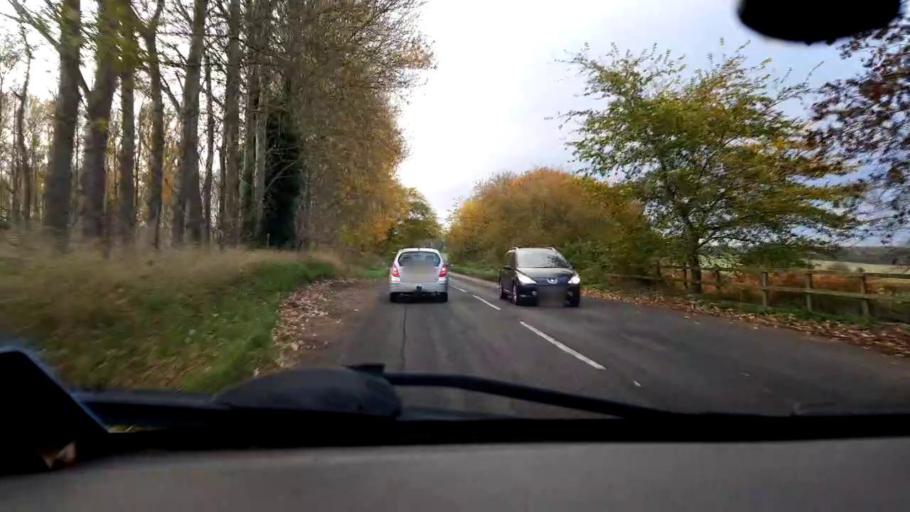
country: GB
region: England
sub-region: Norfolk
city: Horsford
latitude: 52.6891
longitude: 1.2718
